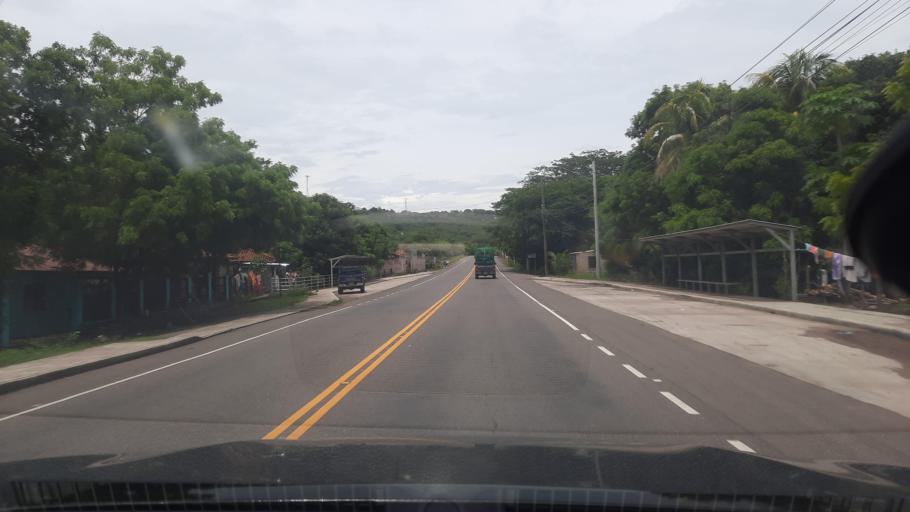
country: HN
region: Valle
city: Goascoran
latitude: 13.5575
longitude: -87.6539
